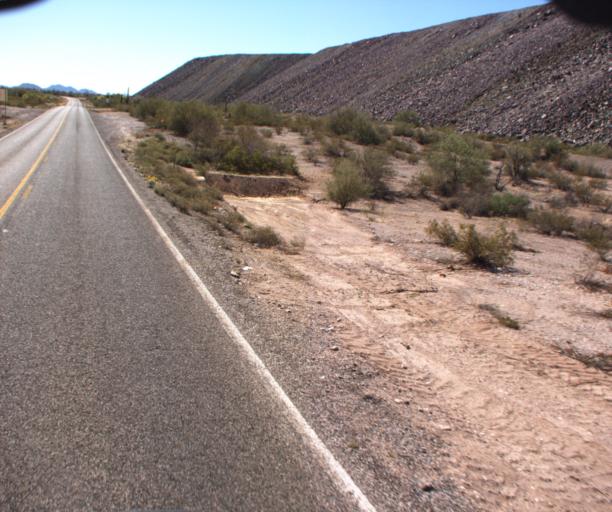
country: US
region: Arizona
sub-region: Pima County
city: Ajo
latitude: 32.3614
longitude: -112.8340
